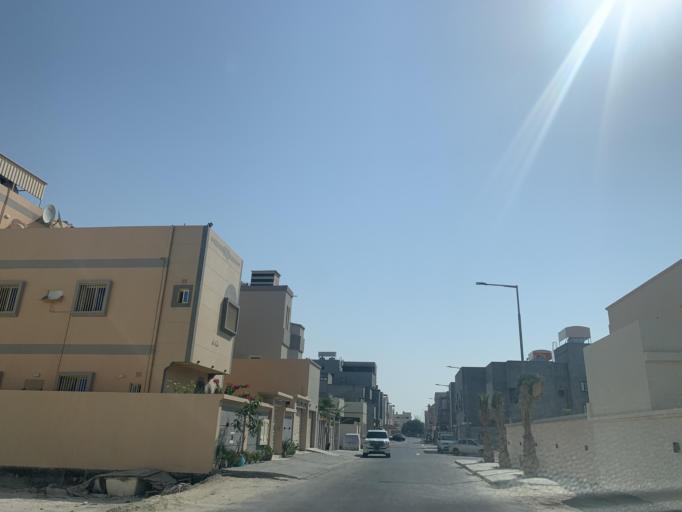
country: BH
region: Central Governorate
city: Madinat Hamad
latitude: 26.1370
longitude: 50.4922
